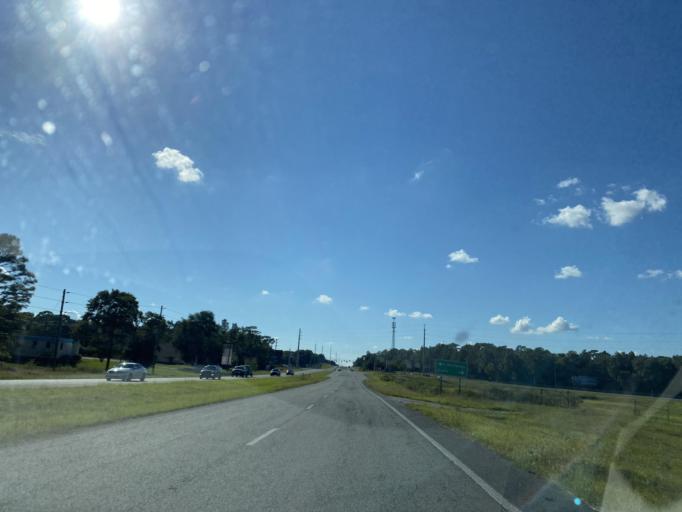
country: US
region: Florida
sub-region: Citrus County
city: Hernando
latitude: 29.0537
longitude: -82.2799
